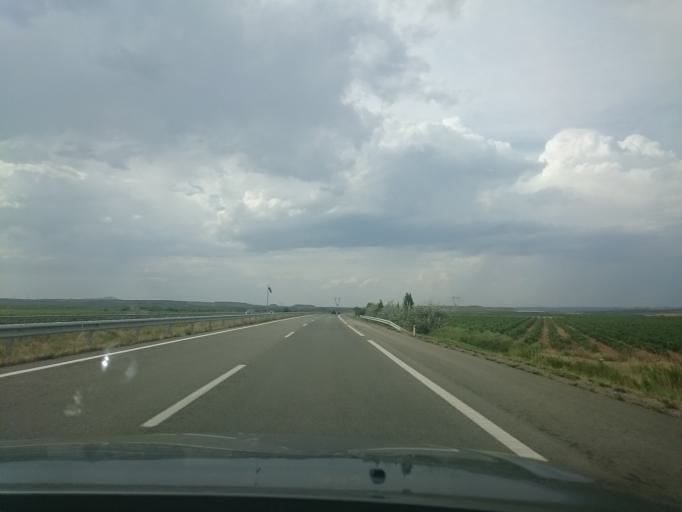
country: ES
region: La Rioja
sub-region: Provincia de La Rioja
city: Rincon de Soto
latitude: 42.1693
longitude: -1.8308
